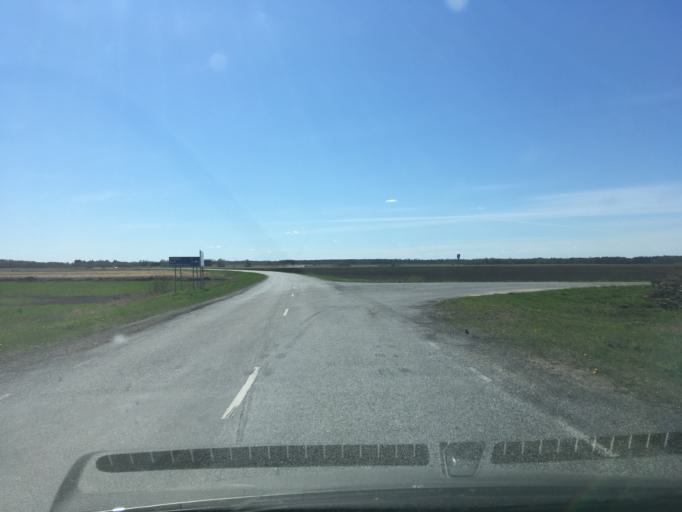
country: EE
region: Harju
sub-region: Raasiku vald
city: Arukula
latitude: 59.4262
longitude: 25.0781
